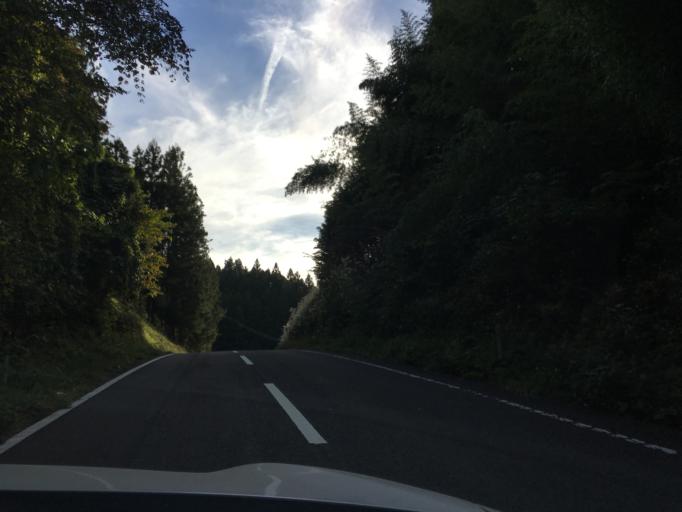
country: JP
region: Fukushima
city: Ishikawa
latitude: 37.2117
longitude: 140.5977
